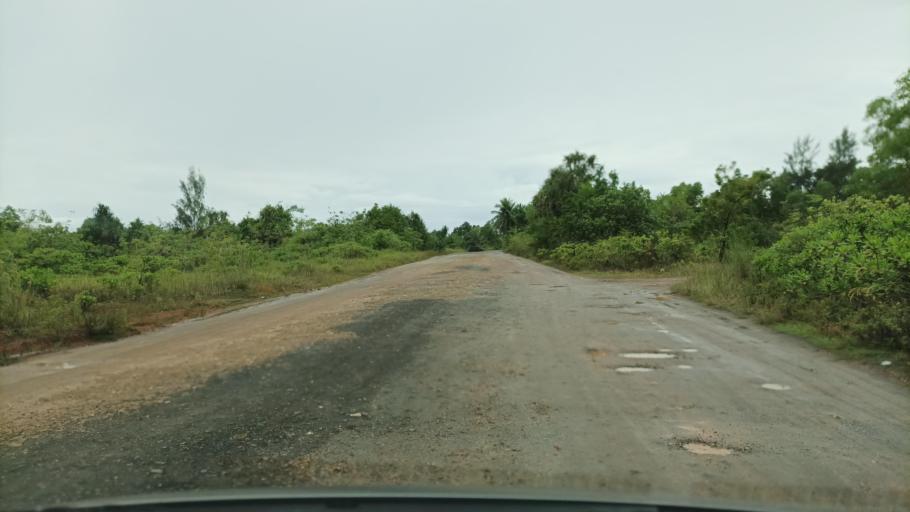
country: FM
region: Yap
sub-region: Weloy Municipality
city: Colonia
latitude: 9.5442
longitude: 138.1659
